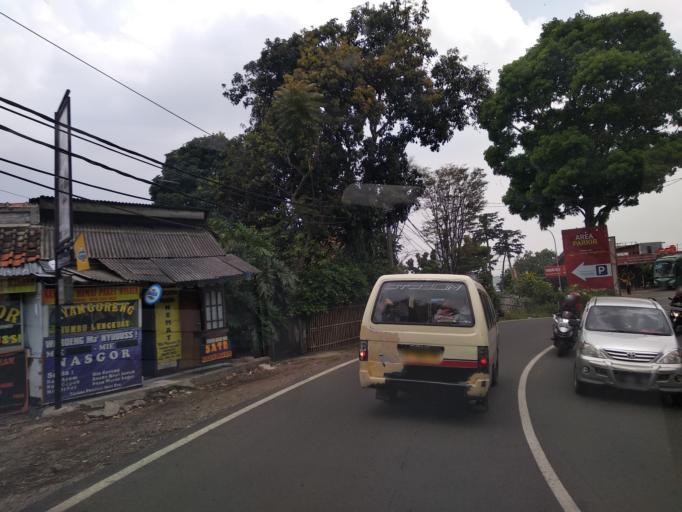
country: ID
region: West Java
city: Lembang
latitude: -6.8347
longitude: 107.6021
